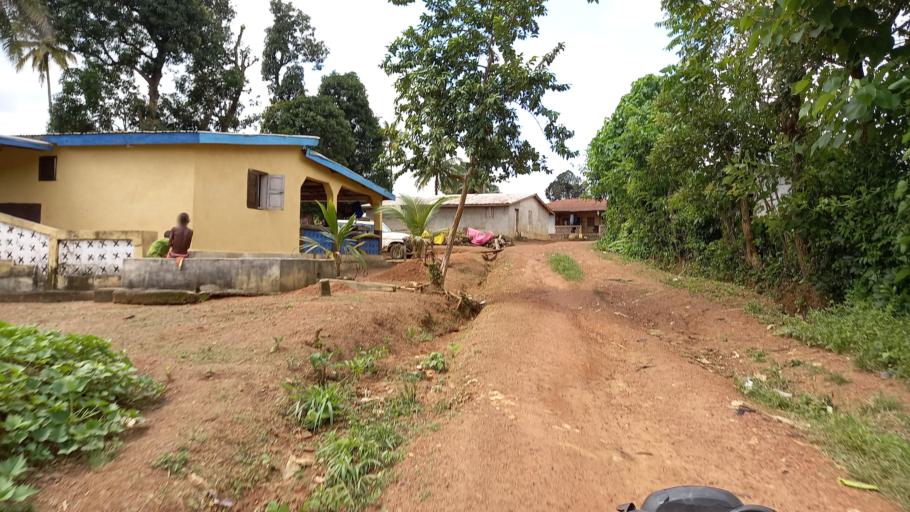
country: SL
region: Northern Province
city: Kamakwie
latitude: 9.5036
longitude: -12.2429
